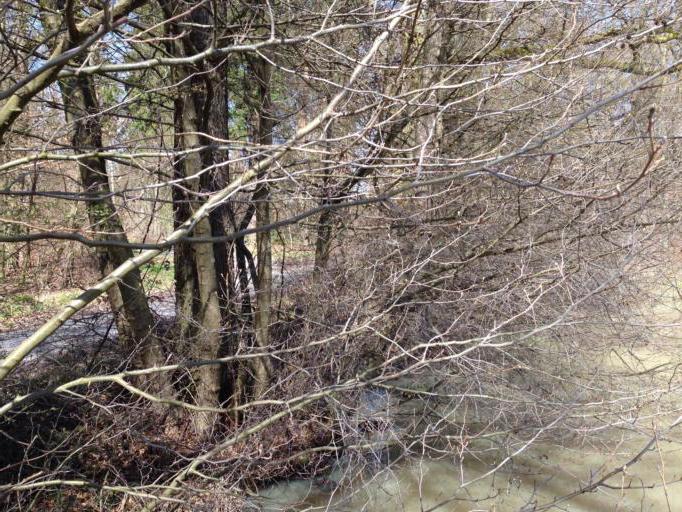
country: DE
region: Baden-Wuerttemberg
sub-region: Karlsruhe Region
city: Illingen
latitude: 49.0037
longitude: 8.9432
